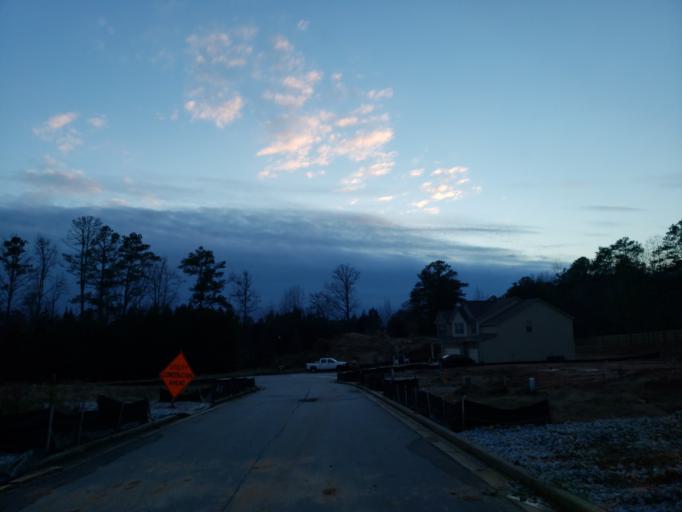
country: US
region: Georgia
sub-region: Fulton County
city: Union City
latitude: 33.6913
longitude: -84.5913
